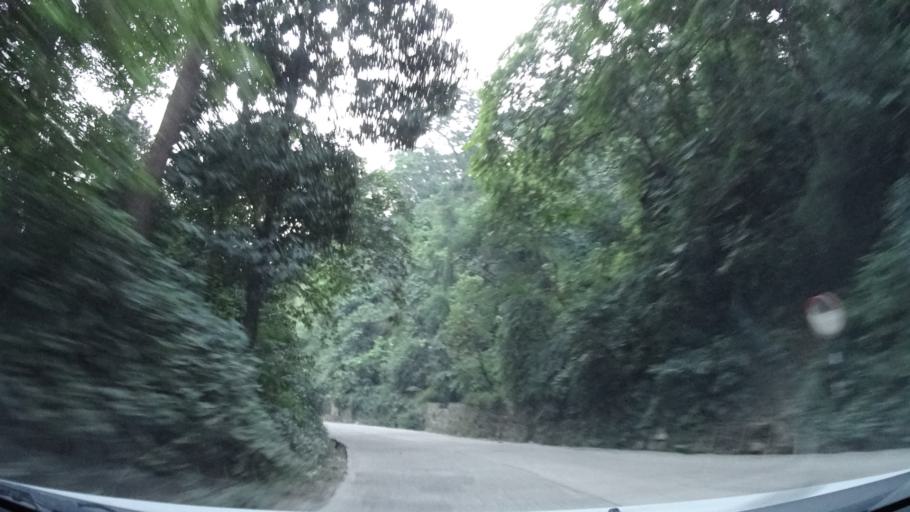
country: IN
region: Uttar Pradesh
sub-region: Maharajganj
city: Nichlaul
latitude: 27.5533
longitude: 83.8279
